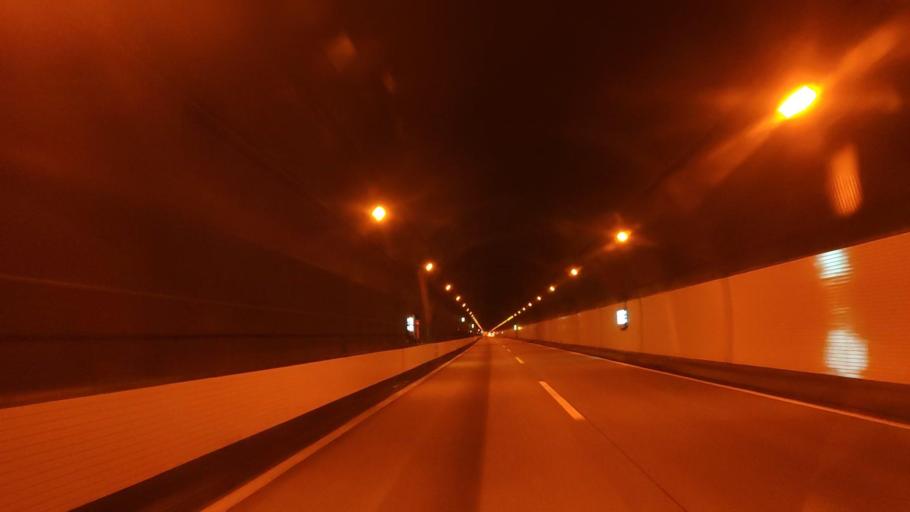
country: JP
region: Toyama
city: Nyuzen
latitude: 36.9803
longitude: 137.6635
